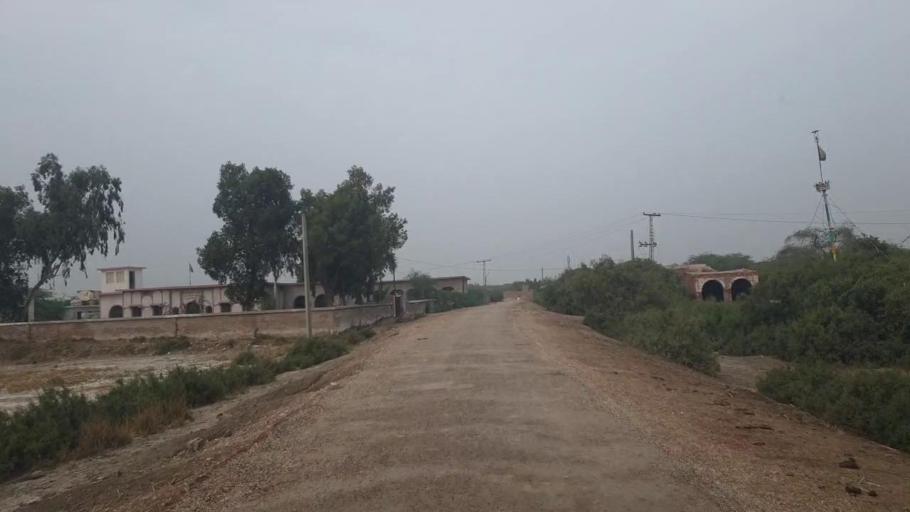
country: PK
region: Sindh
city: Berani
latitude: 25.8085
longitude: 68.7340
